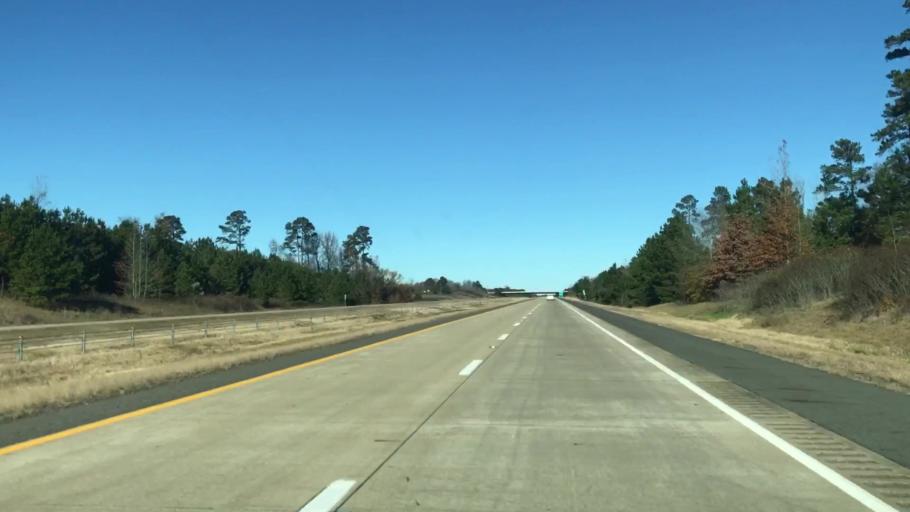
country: US
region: Texas
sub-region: Bowie County
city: Texarkana
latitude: 33.3099
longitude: -93.9390
